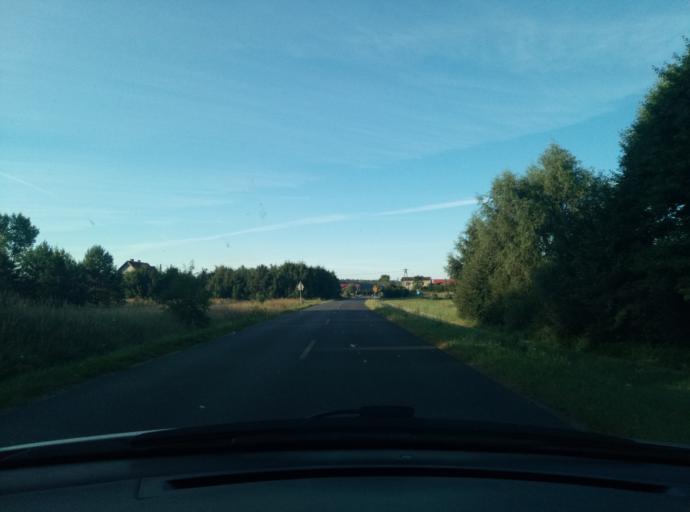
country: PL
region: Kujawsko-Pomorskie
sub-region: Powiat wabrzeski
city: Wabrzezno
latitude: 53.2548
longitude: 18.9330
